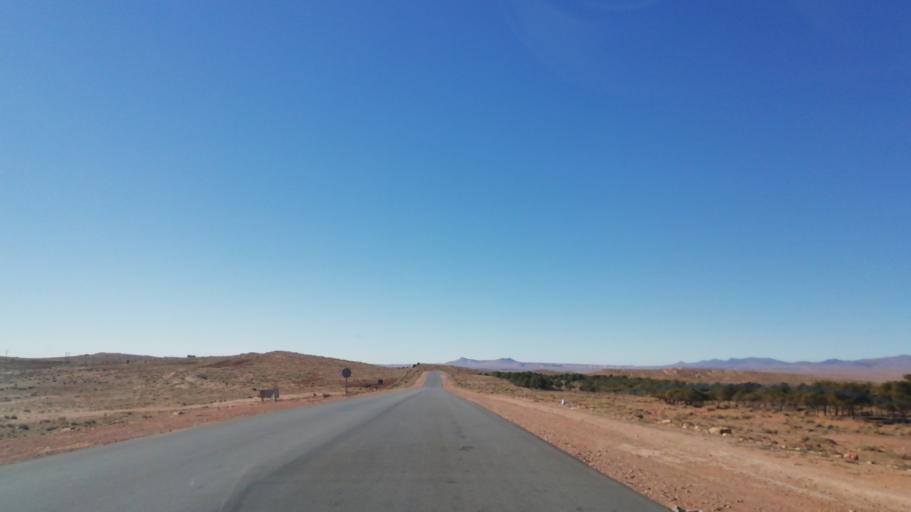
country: DZ
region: El Bayadh
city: El Bayadh
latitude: 33.6416
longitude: 1.3890
